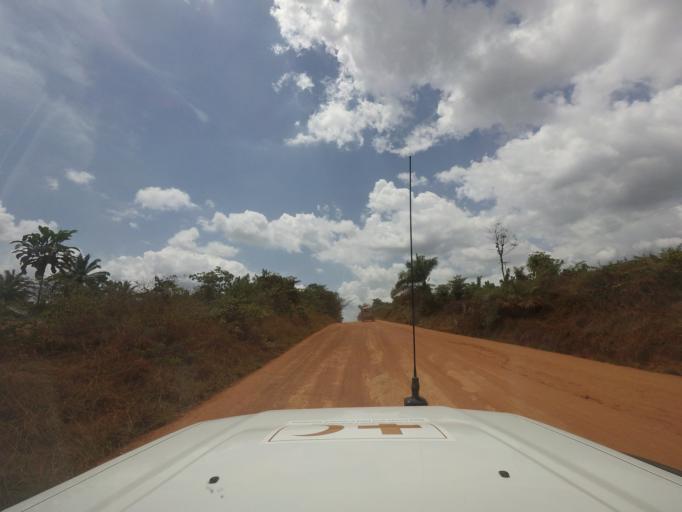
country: LR
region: Nimba
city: Sanniquellie
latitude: 7.2280
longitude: -8.9389
